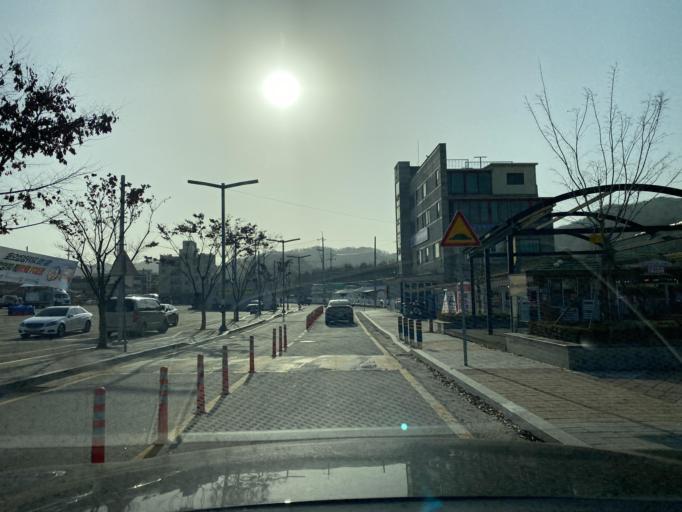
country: KR
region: Chungcheongnam-do
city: Yesan
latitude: 36.6765
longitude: 126.8485
